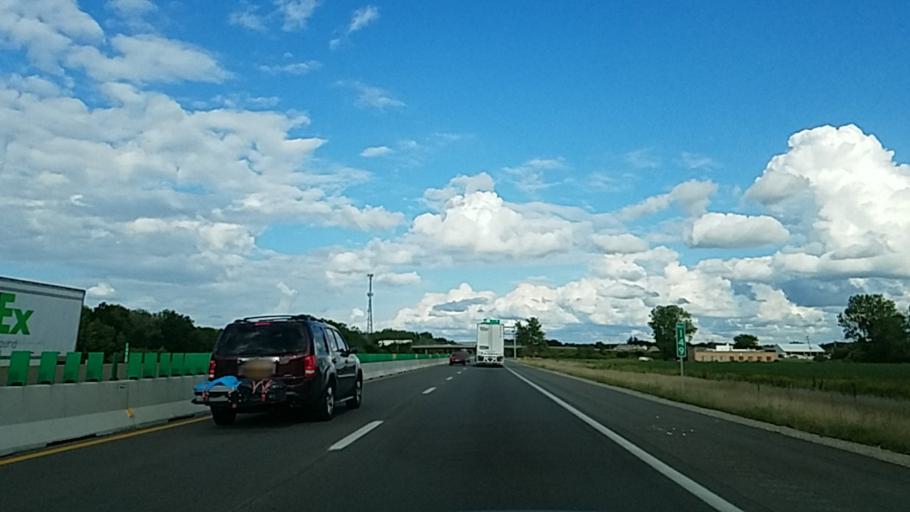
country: US
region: Ohio
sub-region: Lorain County
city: North Ridgeville
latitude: 41.3782
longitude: -82.0491
